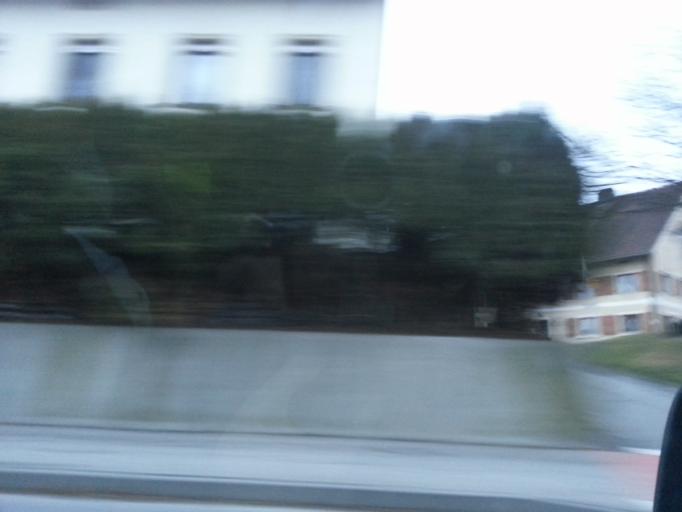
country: DE
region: Baden-Wuerttemberg
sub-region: Tuebingen Region
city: Markdorf
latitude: 47.7022
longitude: 9.3993
